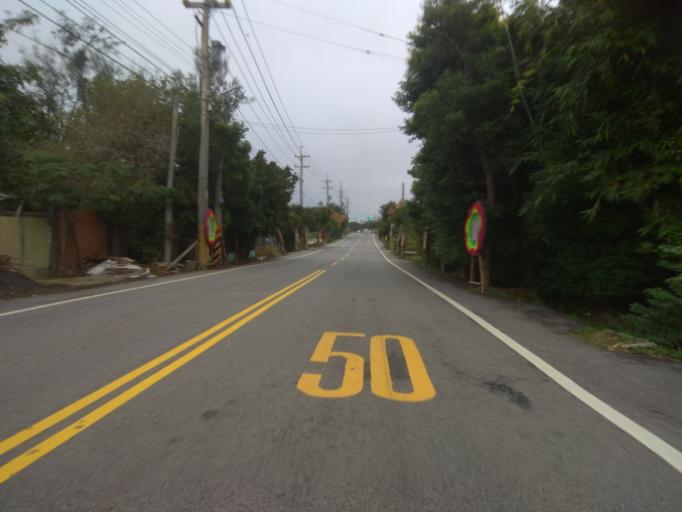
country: TW
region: Taiwan
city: Taoyuan City
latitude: 24.9975
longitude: 121.1186
